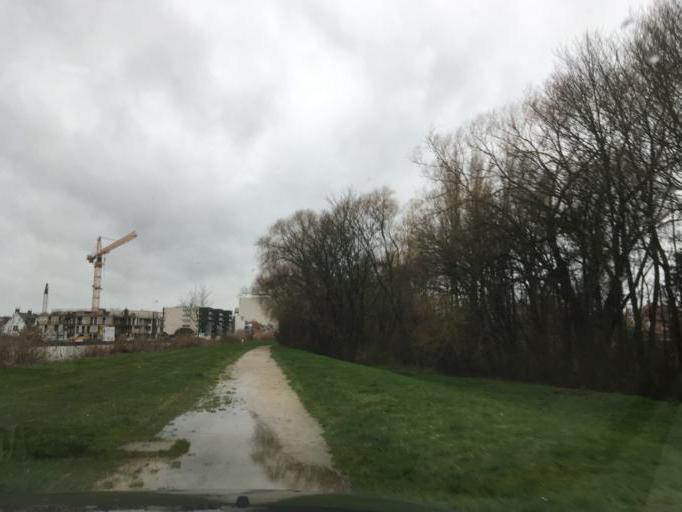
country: BE
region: Flanders
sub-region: Provincie West-Vlaanderen
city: Izegem
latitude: 50.9219
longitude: 3.2231
